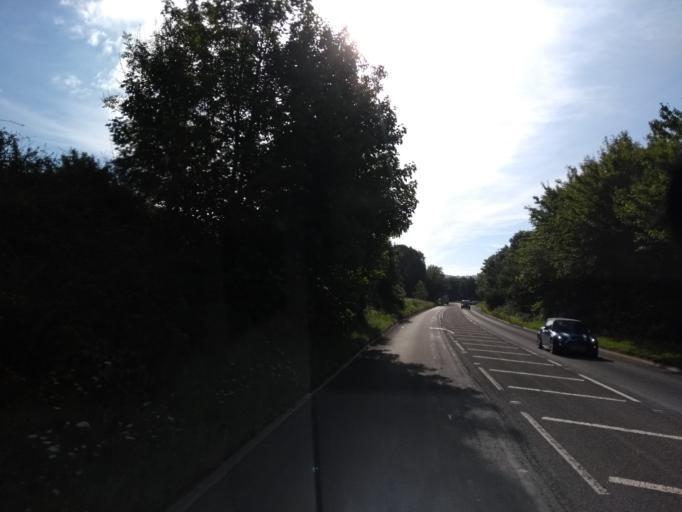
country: GB
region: England
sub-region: Somerset
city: Axbridge
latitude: 51.2886
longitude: -2.8076
